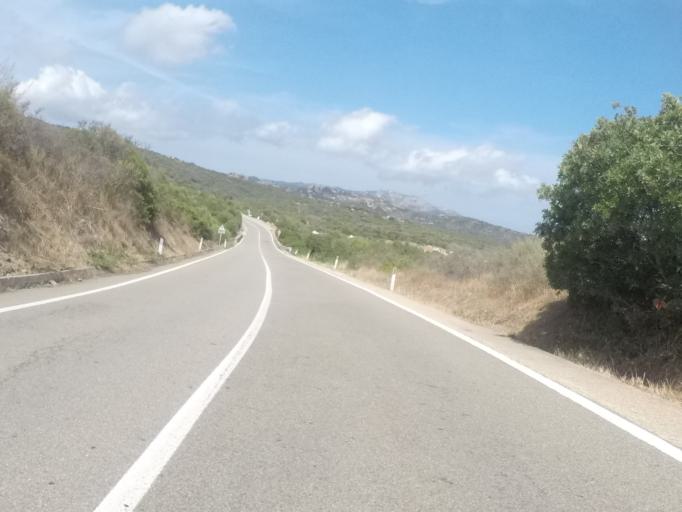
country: IT
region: Sardinia
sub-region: Provincia di Olbia-Tempio
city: Porto Cervo
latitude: 41.0453
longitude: 9.5187
